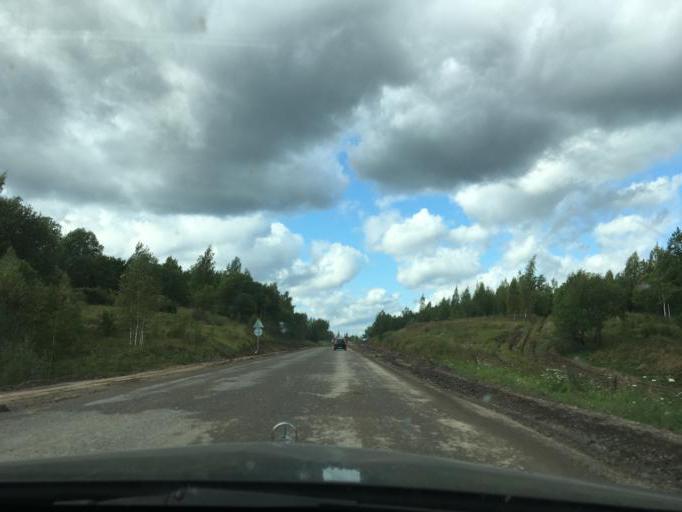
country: RU
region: Pskov
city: Novosokol'niki
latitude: 56.2931
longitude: 30.2378
